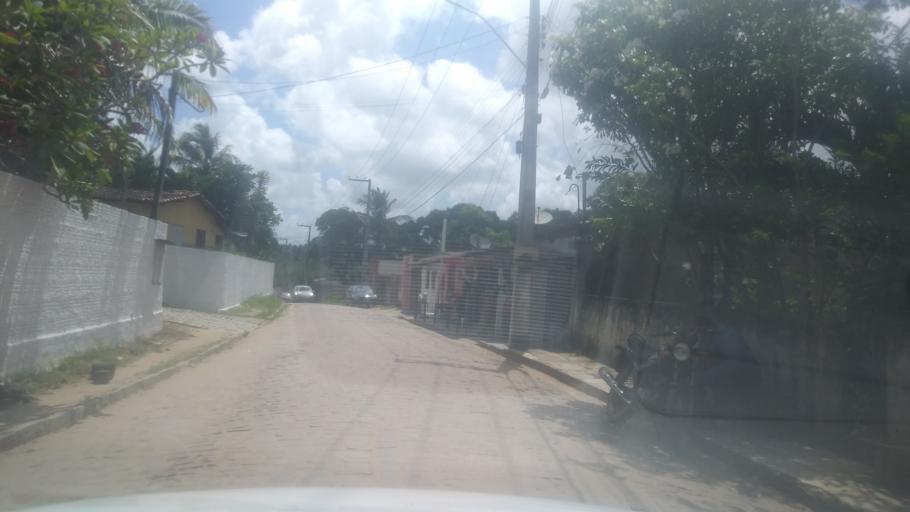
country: BR
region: Rio Grande do Norte
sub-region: Sao Jose De Mipibu
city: Sao Jose de Mipibu
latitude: -6.0720
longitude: -35.2311
